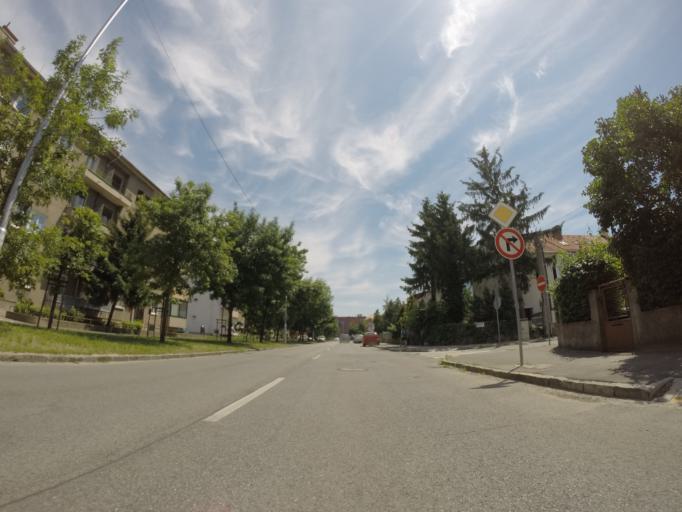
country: SK
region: Bratislavsky
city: Bratislava
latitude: 48.1708
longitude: 17.1361
